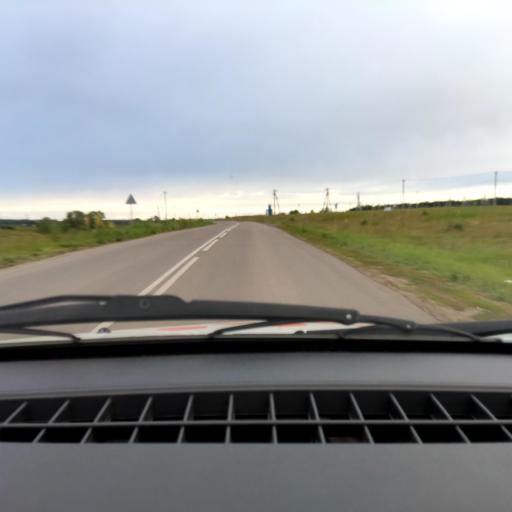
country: RU
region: Bashkortostan
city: Avdon
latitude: 54.5596
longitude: 55.7634
